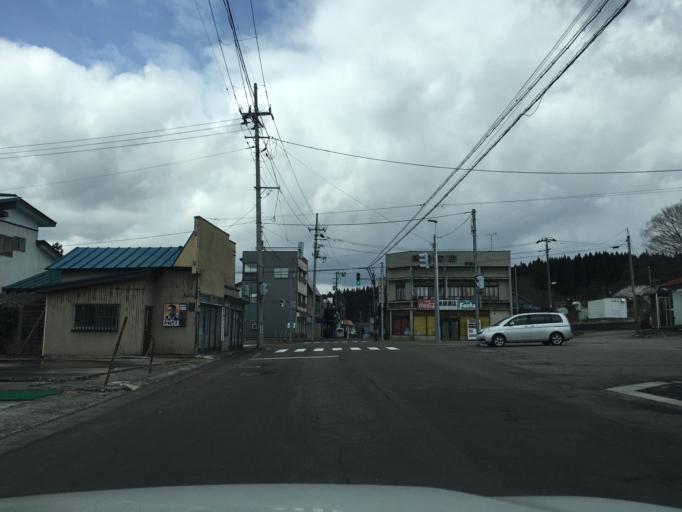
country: JP
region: Akita
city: Takanosu
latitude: 40.1606
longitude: 140.3303
